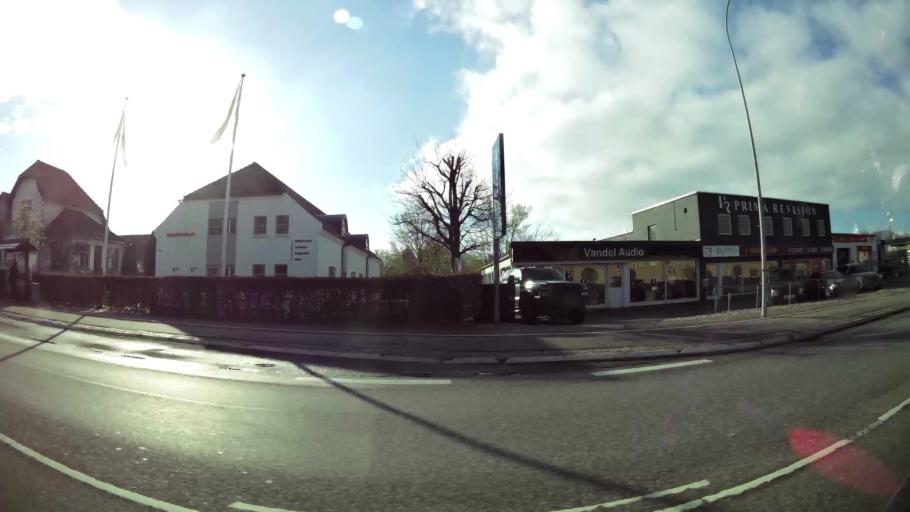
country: DK
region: Zealand
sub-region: Roskilde Kommune
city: Roskilde
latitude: 55.6290
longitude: 12.0665
